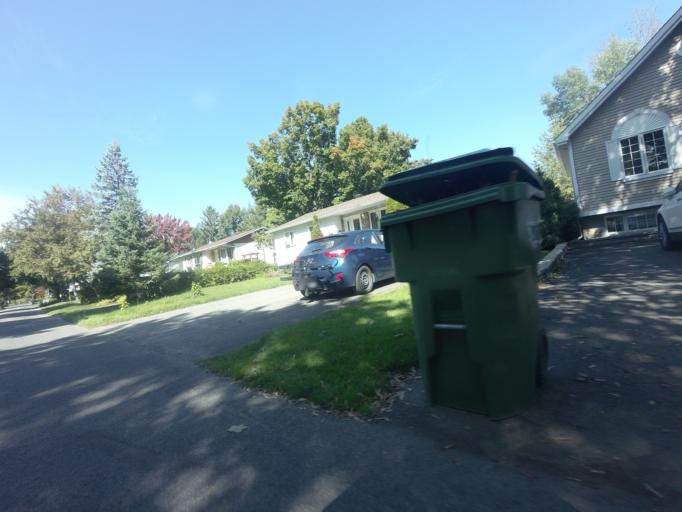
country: CA
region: Quebec
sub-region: Laurentides
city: Saint-Eustache
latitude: 45.5544
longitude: -73.9058
